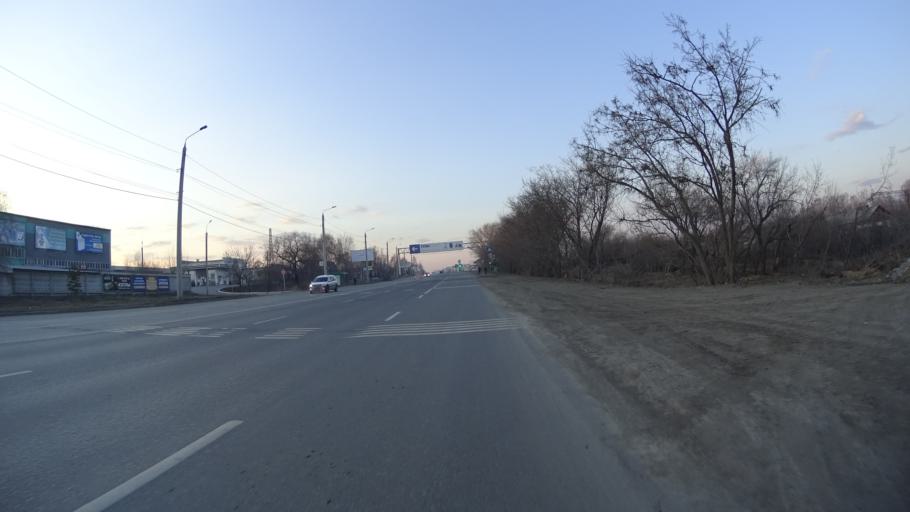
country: RU
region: Chelyabinsk
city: Novosineglazovskiy
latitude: 55.0852
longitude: 61.3883
